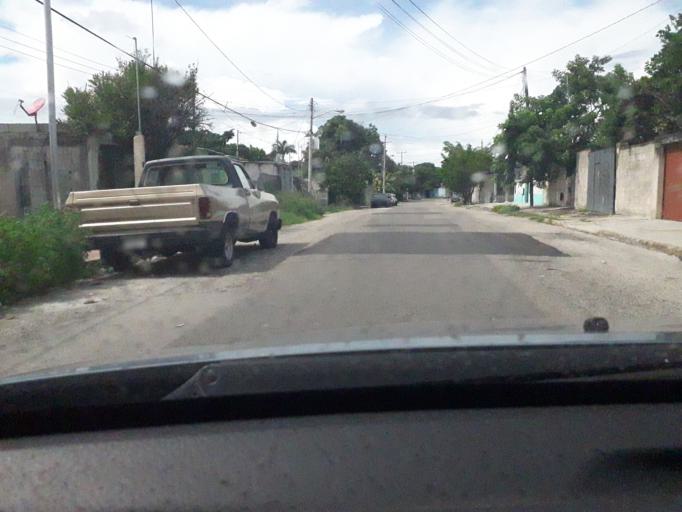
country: MX
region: Yucatan
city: Merida
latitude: 20.9656
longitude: -89.6586
